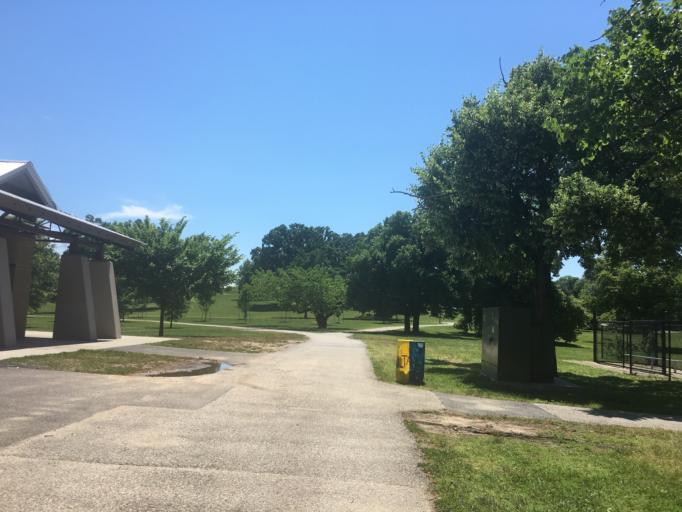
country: US
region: Maryland
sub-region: City of Baltimore
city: Baltimore
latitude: 39.2805
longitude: -76.6400
